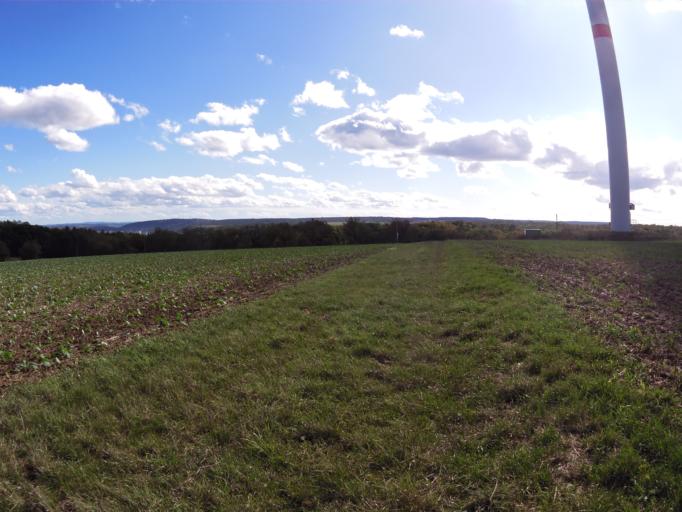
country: DE
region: Bavaria
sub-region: Regierungsbezirk Unterfranken
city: Erlabrunn
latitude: 49.8332
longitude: 9.8342
